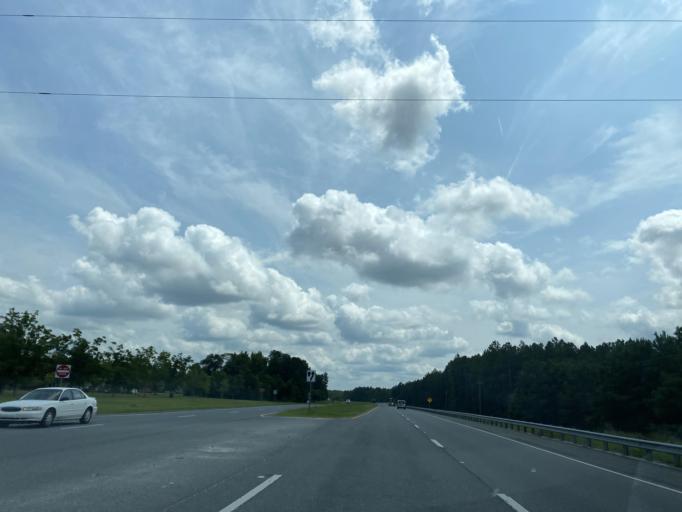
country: US
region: Georgia
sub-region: Ware County
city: Deenwood
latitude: 31.3358
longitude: -82.4639
